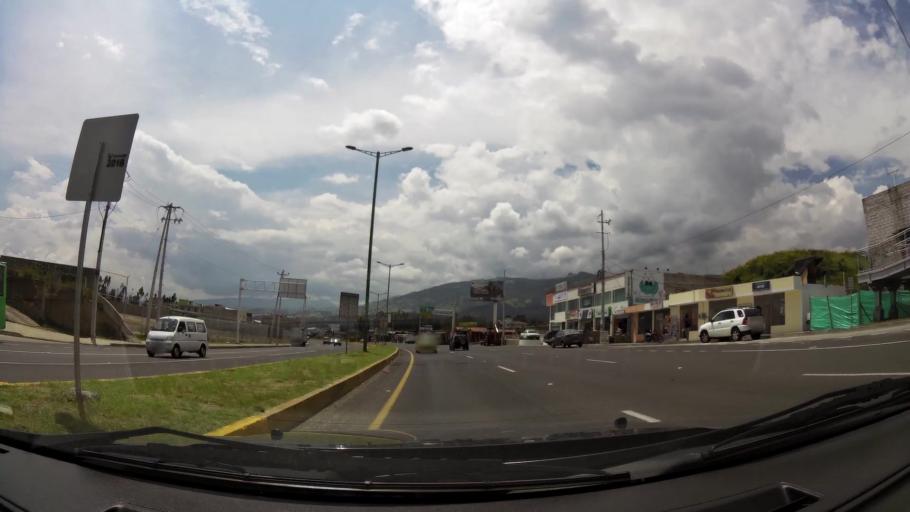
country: EC
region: Pichincha
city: Sangolqui
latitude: -0.2233
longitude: -78.3409
